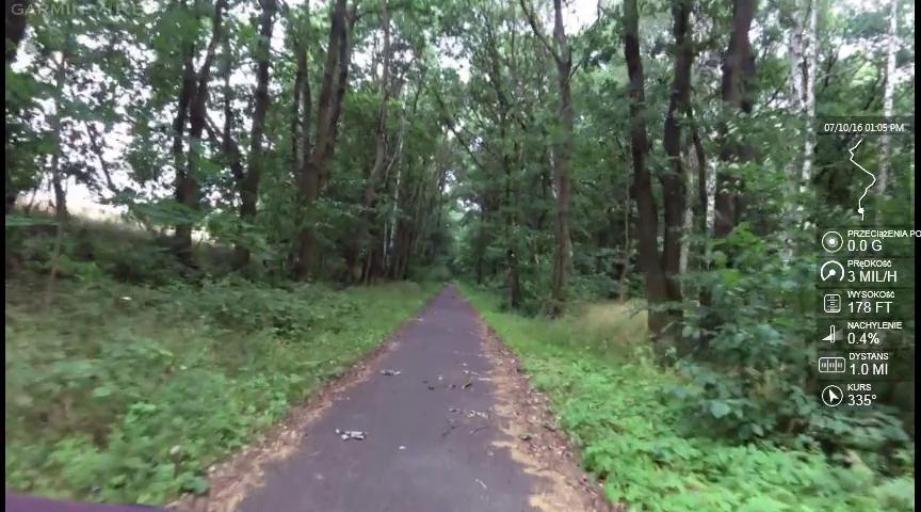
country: PL
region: West Pomeranian Voivodeship
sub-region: Powiat gryfinski
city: Banie
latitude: 53.0521
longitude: 14.6290
